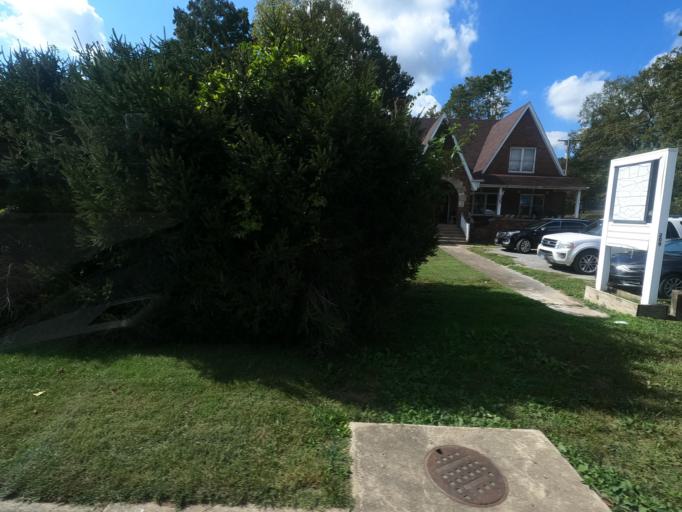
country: US
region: Illinois
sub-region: Johnson County
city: Vienna
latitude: 37.4163
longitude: -88.8932
